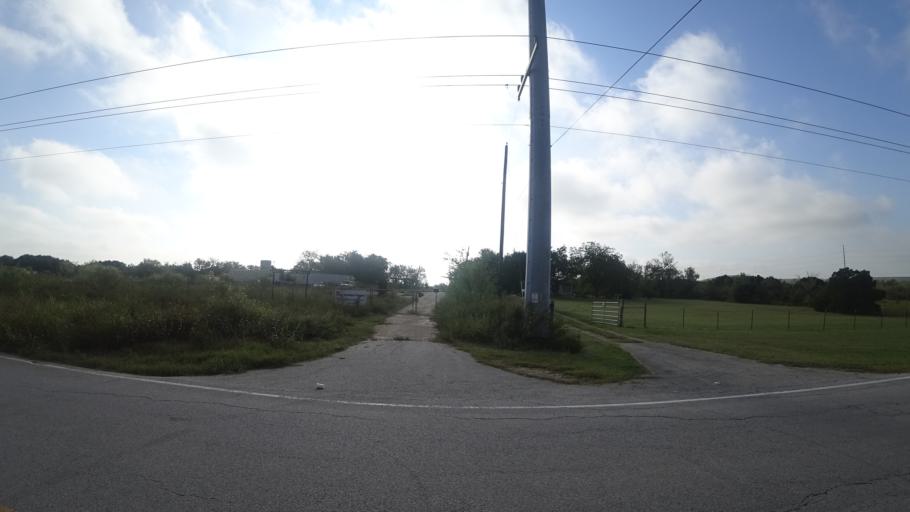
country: US
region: Texas
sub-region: Travis County
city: Manor
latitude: 30.3554
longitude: -97.6360
